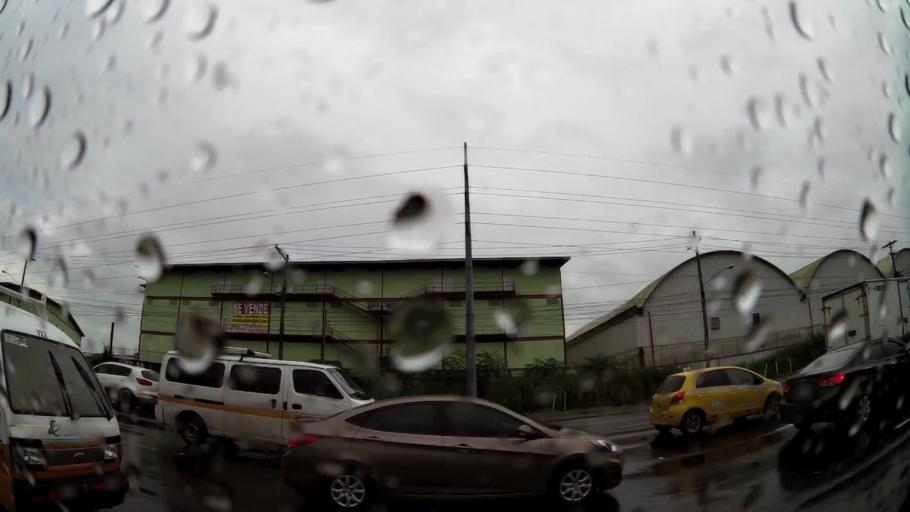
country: PA
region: Colon
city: Arco Iris
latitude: 9.3402
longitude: -79.8769
